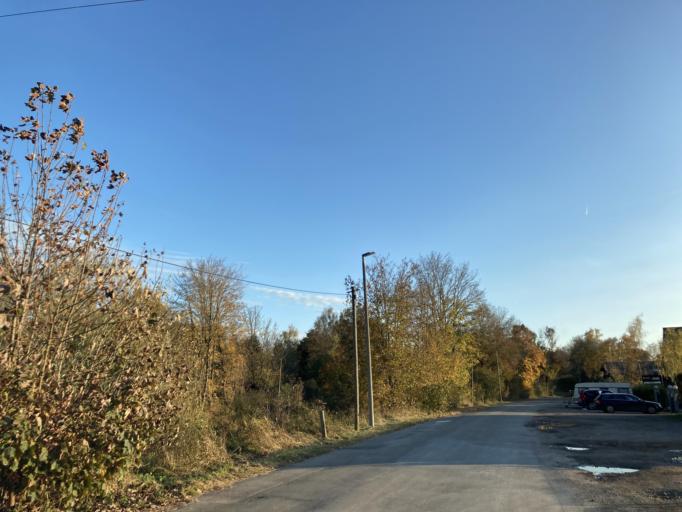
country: DE
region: Baden-Wuerttemberg
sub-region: Freiburg Region
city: Villingen-Schwenningen
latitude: 48.0442
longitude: 8.4686
